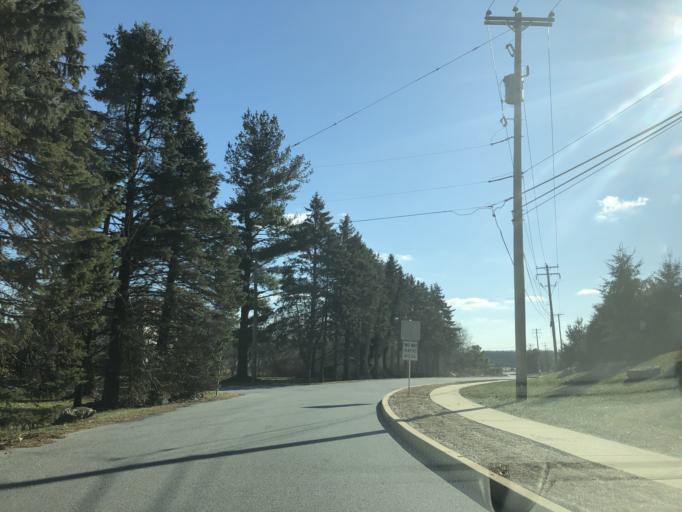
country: US
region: Pennsylvania
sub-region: Chester County
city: Coatesville
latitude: 39.9859
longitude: -75.8753
